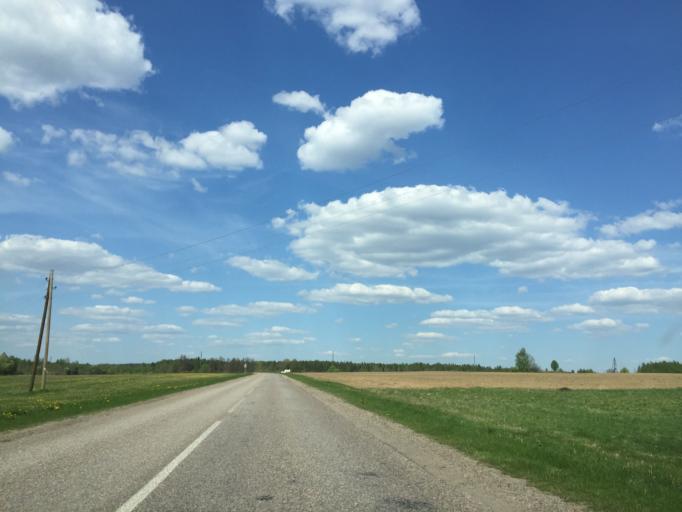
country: LV
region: Limbazu Rajons
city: Limbazi
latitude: 57.3831
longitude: 24.6859
